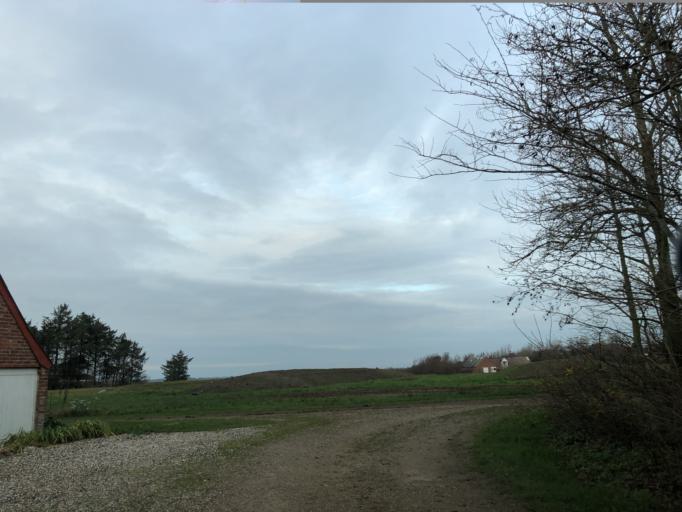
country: DK
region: Central Jutland
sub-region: Holstebro Kommune
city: Ulfborg
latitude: 56.2763
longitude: 8.2222
